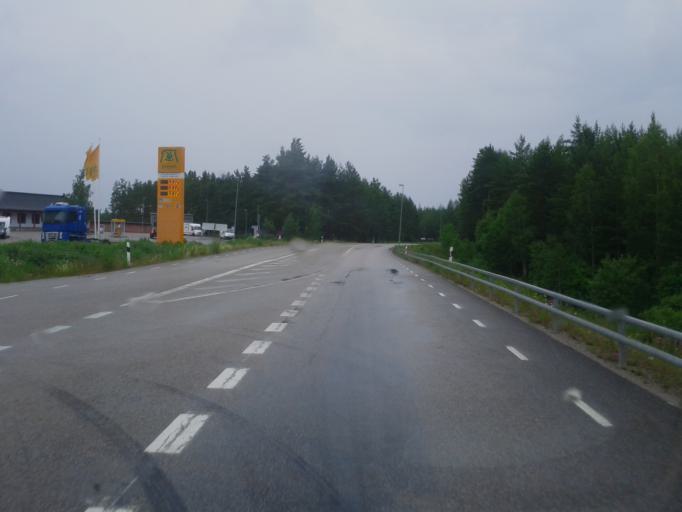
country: SE
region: Uppsala
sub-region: Alvkarleby Kommun
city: AElvkarleby
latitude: 60.4626
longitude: 17.4174
